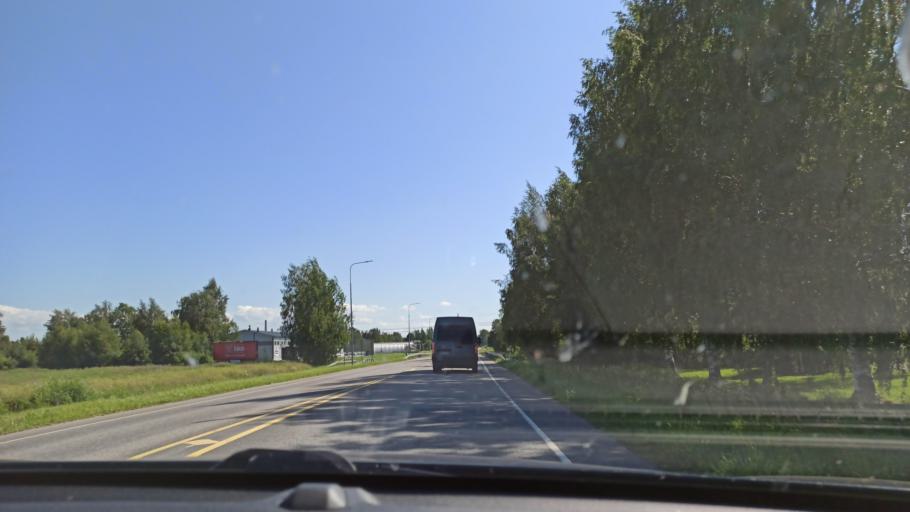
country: FI
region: Satakunta
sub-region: Pori
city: Pori
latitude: 61.5112
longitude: 21.8033
